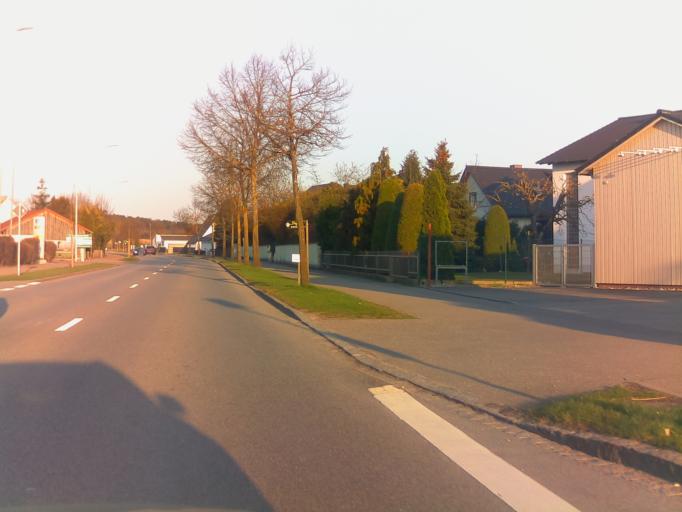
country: DE
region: Bavaria
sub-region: Lower Bavaria
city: Biburg
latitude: 48.8087
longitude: 11.8985
